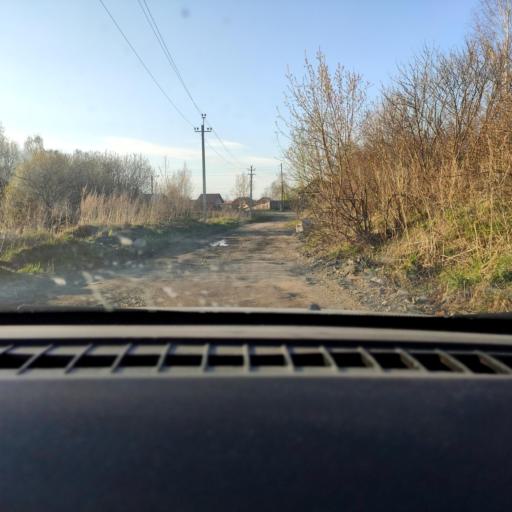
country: RU
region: Perm
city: Perm
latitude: 58.0259
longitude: 56.2105
